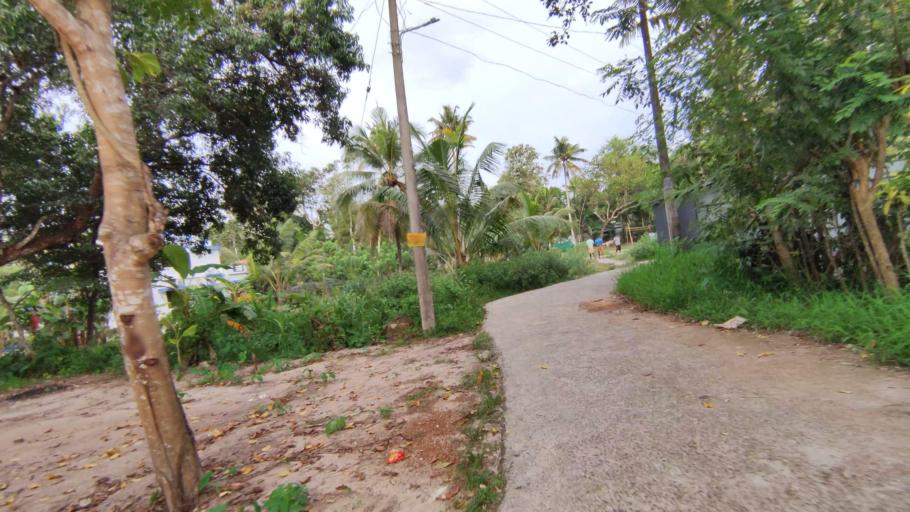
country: IN
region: Kerala
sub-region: Alappuzha
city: Shertallai
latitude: 9.6111
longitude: 76.3498
